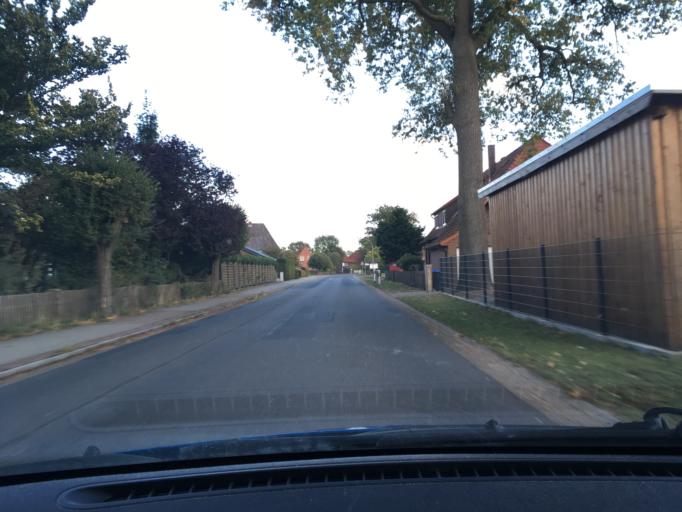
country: DE
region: Lower Saxony
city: Bleckede
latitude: 53.3079
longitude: 10.6930
